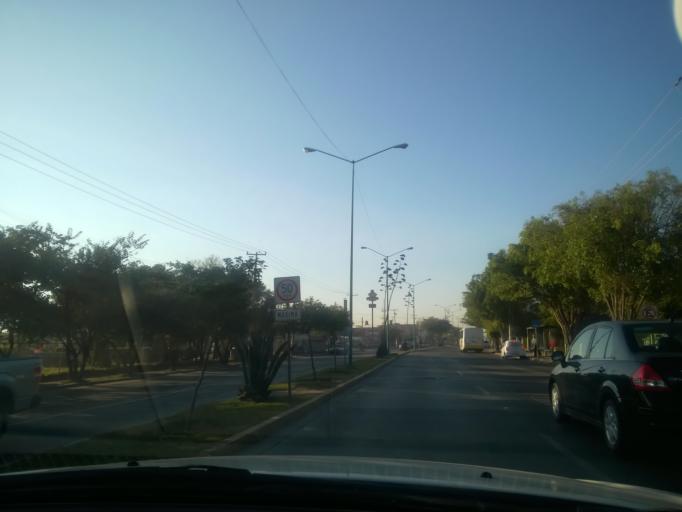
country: MX
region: Guanajuato
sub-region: Leon
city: San Jose de Duran (Los Troncoso)
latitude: 21.0937
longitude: -101.6641
